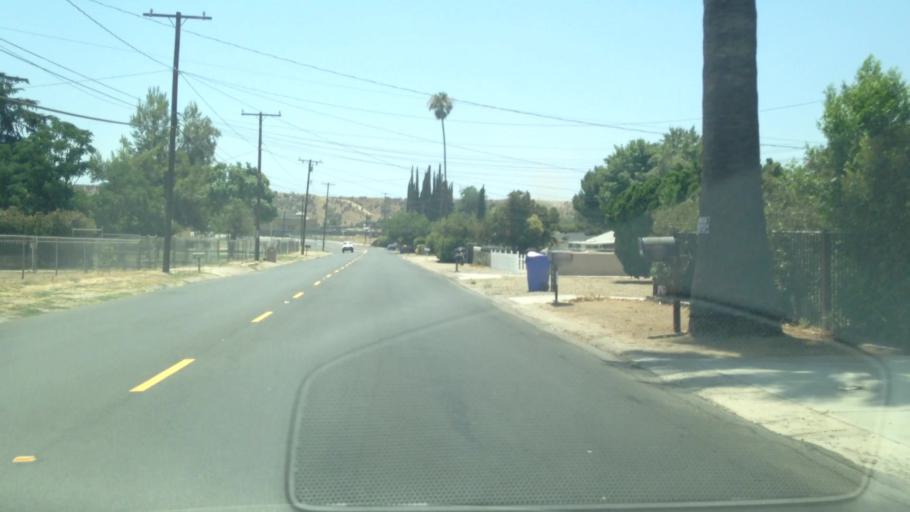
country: US
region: California
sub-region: Riverside County
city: Calimesa
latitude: 34.0221
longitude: -117.0955
